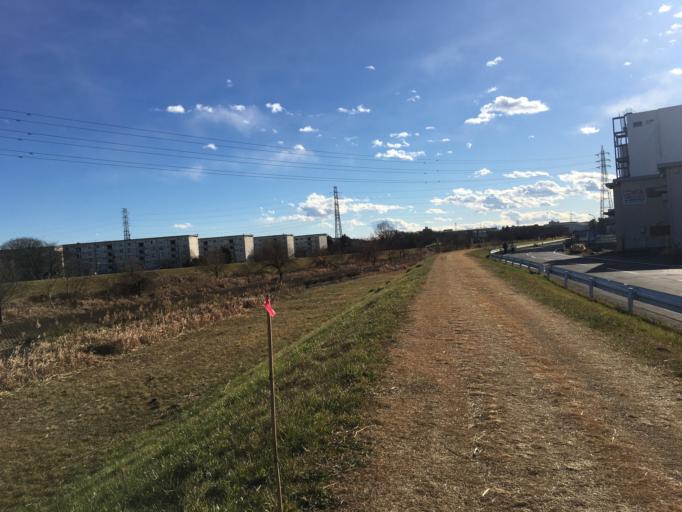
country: JP
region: Saitama
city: Shiki
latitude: 35.8231
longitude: 139.5536
